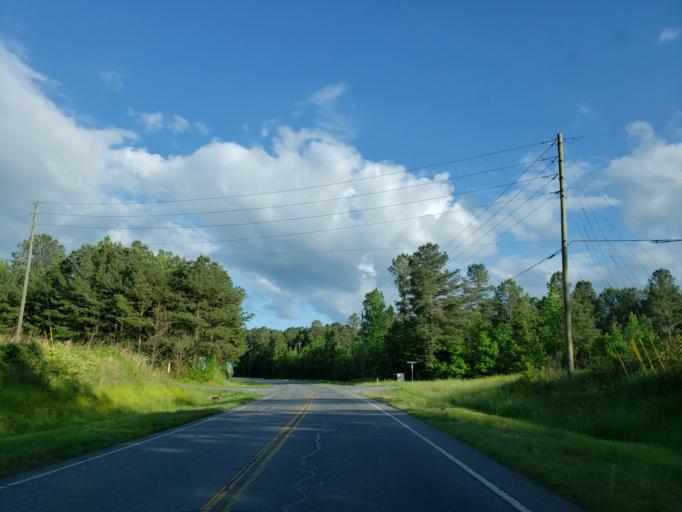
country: US
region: Georgia
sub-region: Bartow County
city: Rydal
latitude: 34.3405
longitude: -84.7430
